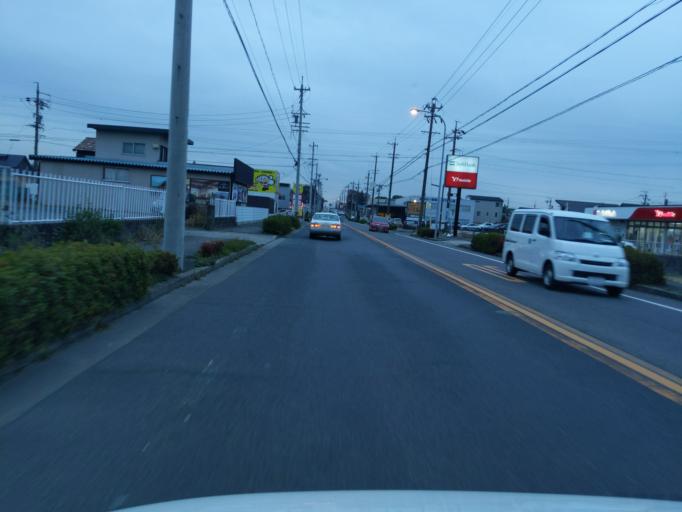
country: JP
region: Aichi
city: Kasugai
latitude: 35.2648
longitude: 136.9724
